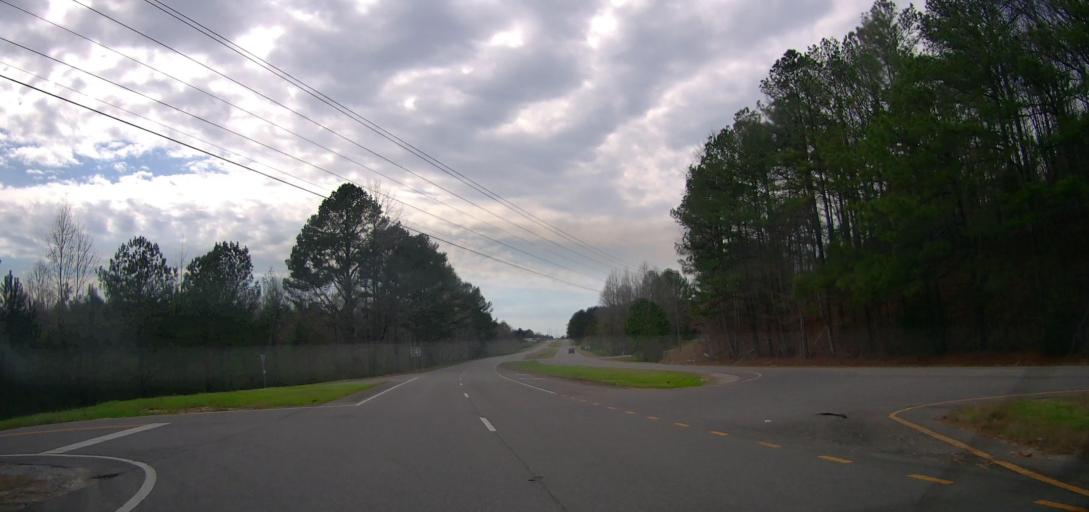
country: US
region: Alabama
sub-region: Marion County
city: Winfield
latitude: 33.9286
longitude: -87.7592
